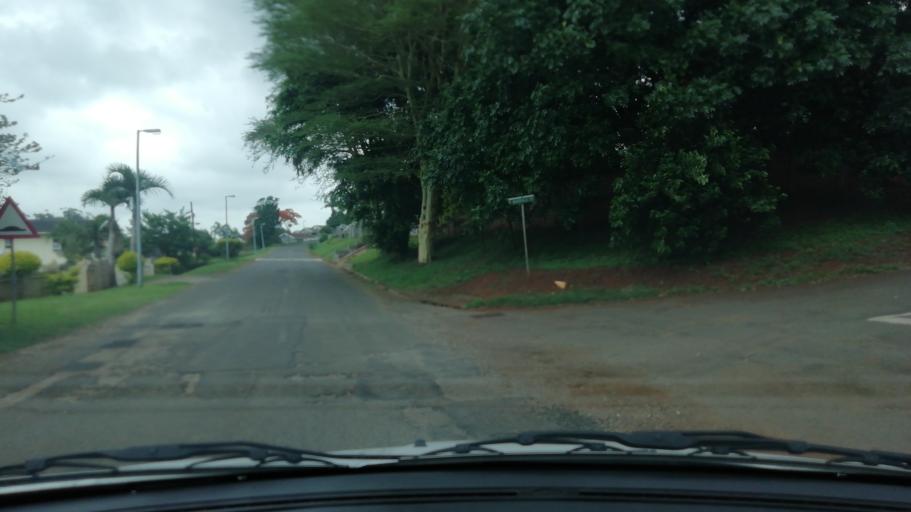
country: ZA
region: KwaZulu-Natal
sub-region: uThungulu District Municipality
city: Empangeni
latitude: -28.7686
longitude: 31.9008
